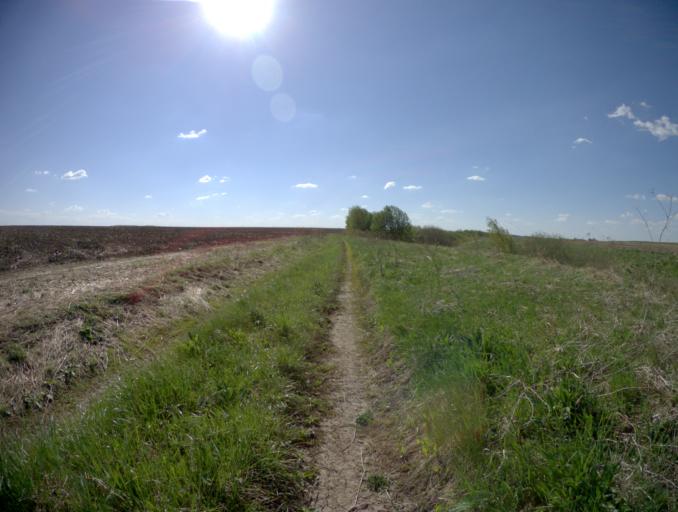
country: RU
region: Vladimir
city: Suzdal'
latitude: 56.3070
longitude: 40.2801
